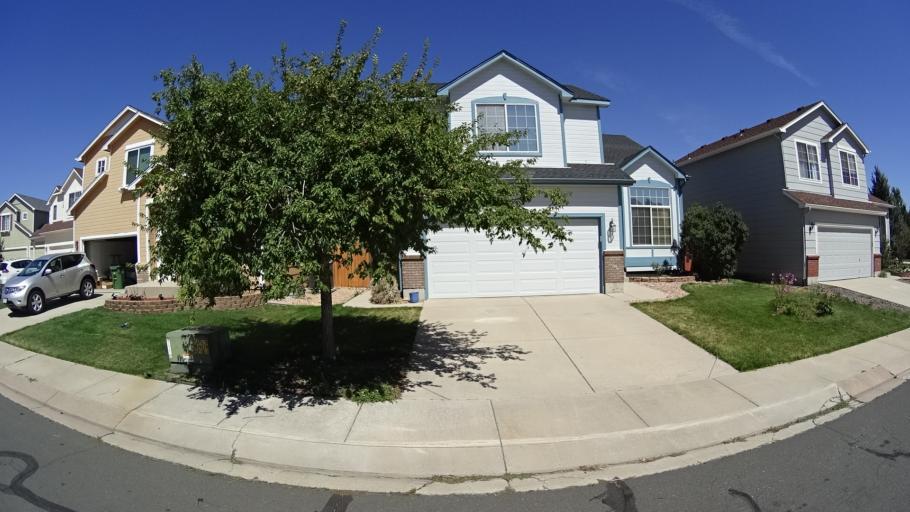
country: US
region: Colorado
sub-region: El Paso County
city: Black Forest
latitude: 38.9482
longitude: -104.7599
